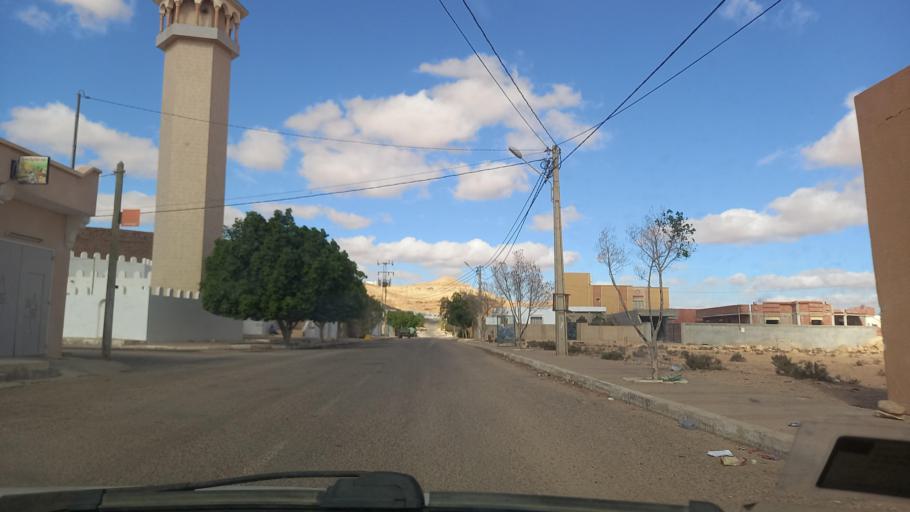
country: TN
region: Tataouine
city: Tataouine
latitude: 32.9807
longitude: 10.2679
